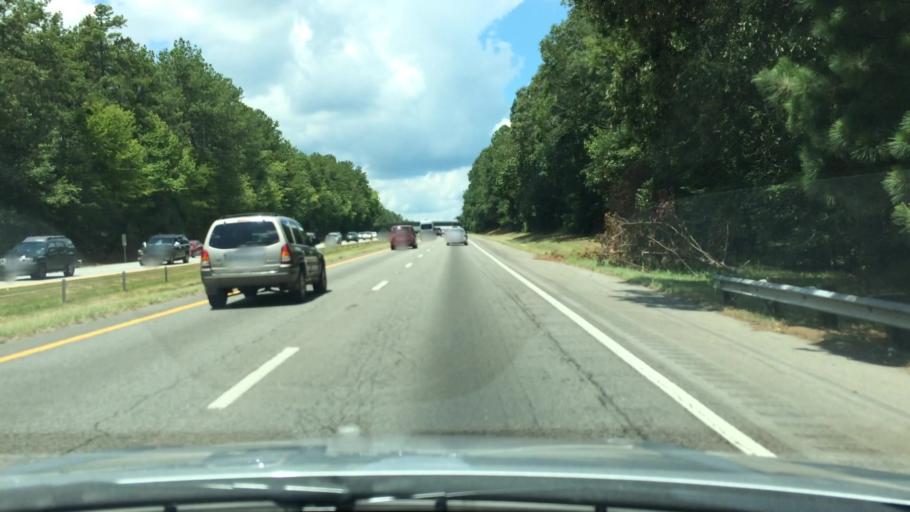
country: US
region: South Carolina
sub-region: Lexington County
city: Chapin
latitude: 34.1902
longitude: -81.3448
